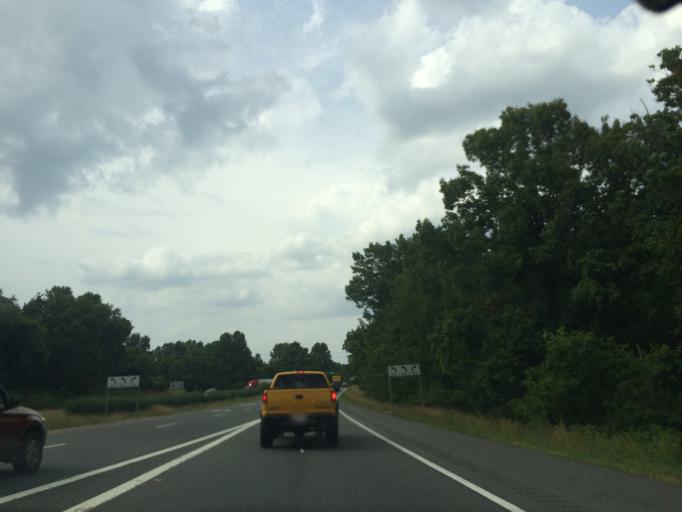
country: US
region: Maryland
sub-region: Howard County
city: Ellicott City
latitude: 39.3007
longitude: -76.8248
